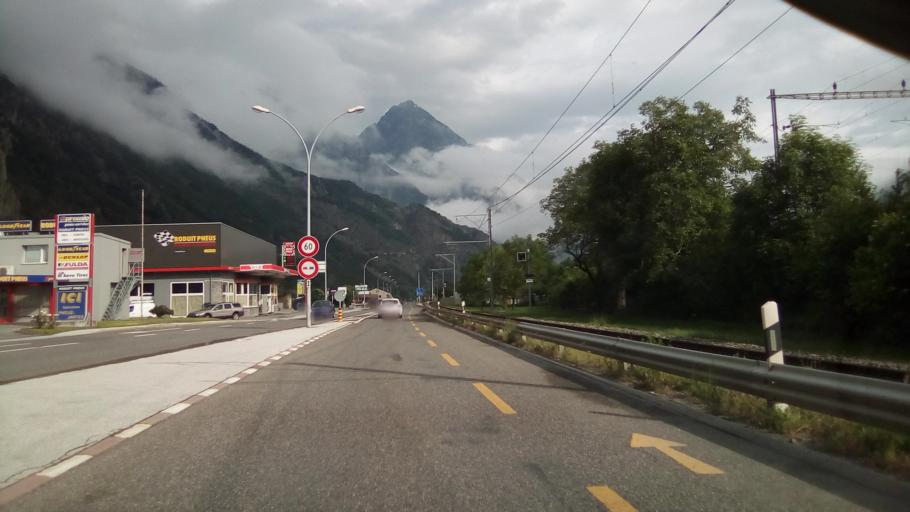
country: CH
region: Valais
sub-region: Martigny District
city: Martigny-Ville
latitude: 46.1084
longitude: 7.0674
